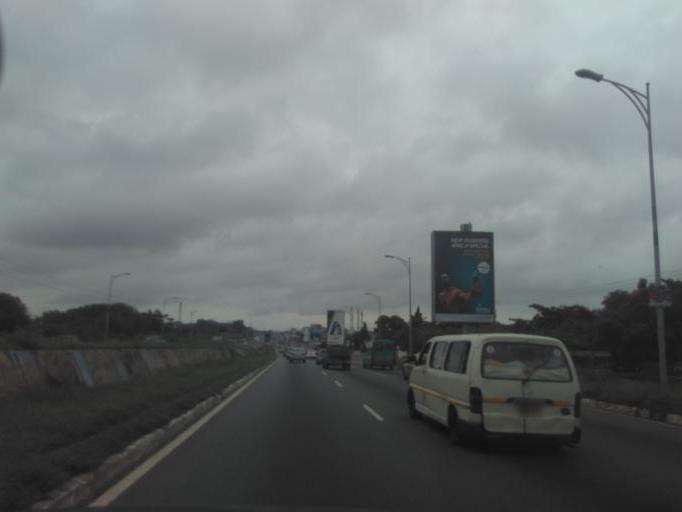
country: GH
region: Greater Accra
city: Medina Estates
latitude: 5.6366
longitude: -0.1773
